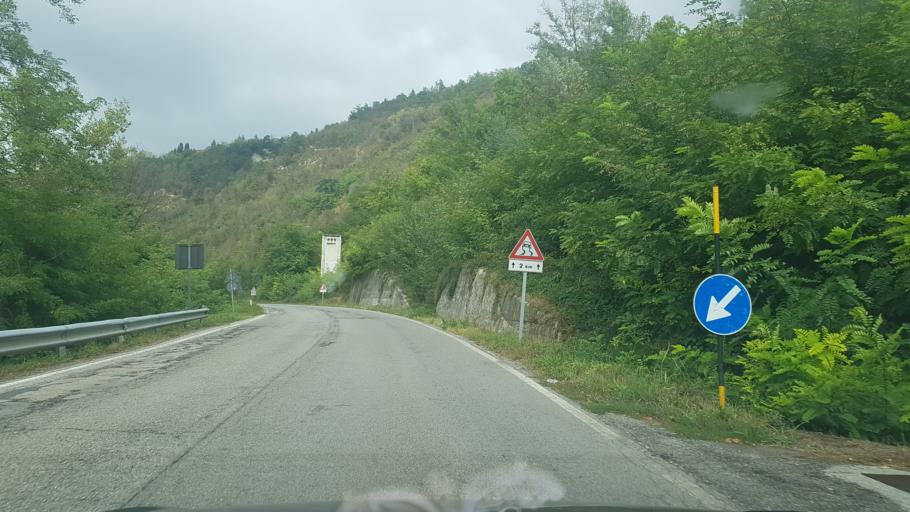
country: IT
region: Piedmont
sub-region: Provincia di Cuneo
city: Monesiglio
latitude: 44.4693
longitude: 8.1172
